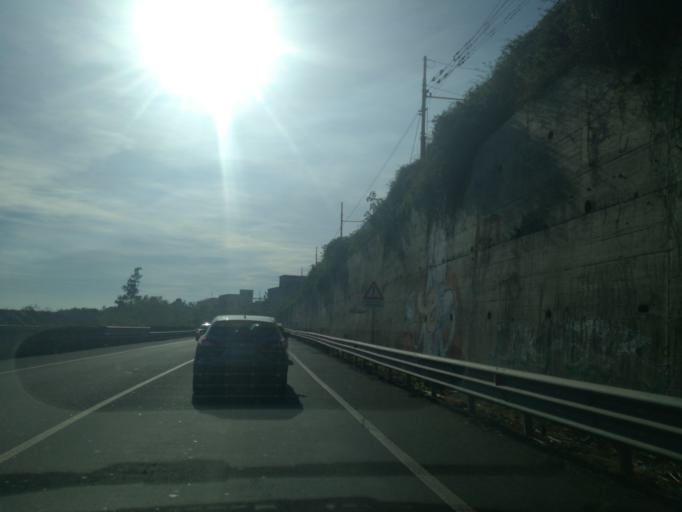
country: IT
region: Sicily
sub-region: Catania
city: Acireale
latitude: 37.6115
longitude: 15.1703
